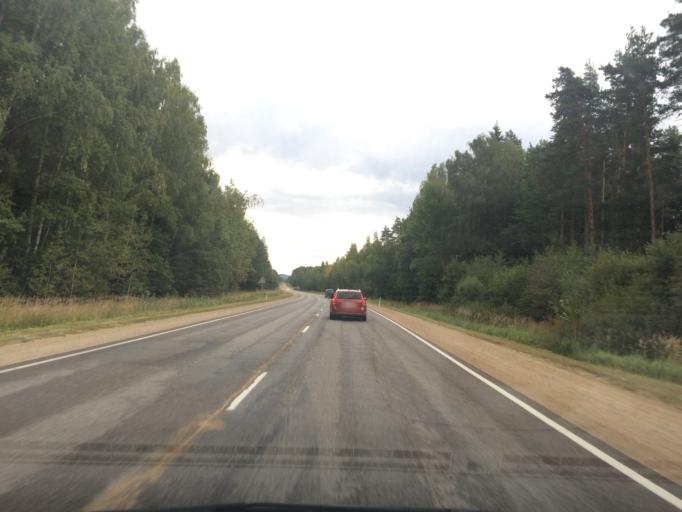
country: LV
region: Koknese
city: Koknese
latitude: 56.5889
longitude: 25.5672
